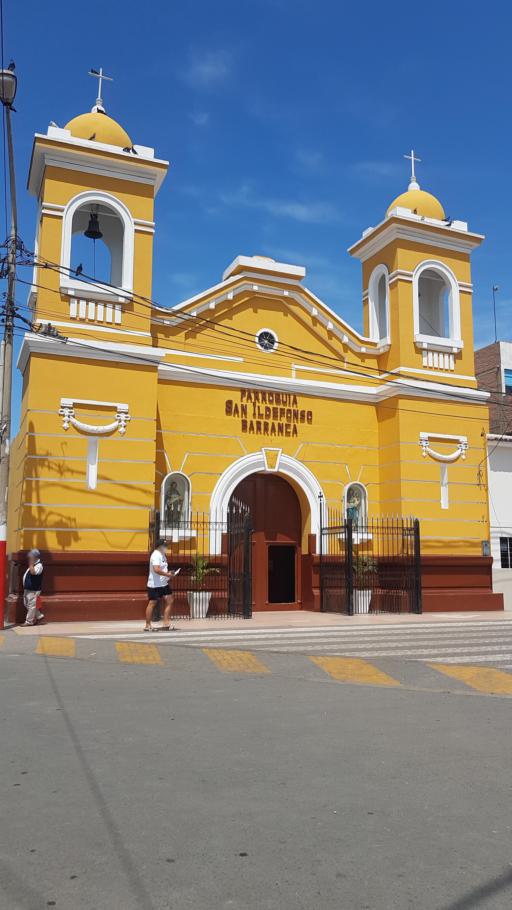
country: PE
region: Lima
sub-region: Barranca
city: Barranca
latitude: -10.7544
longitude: -77.7608
